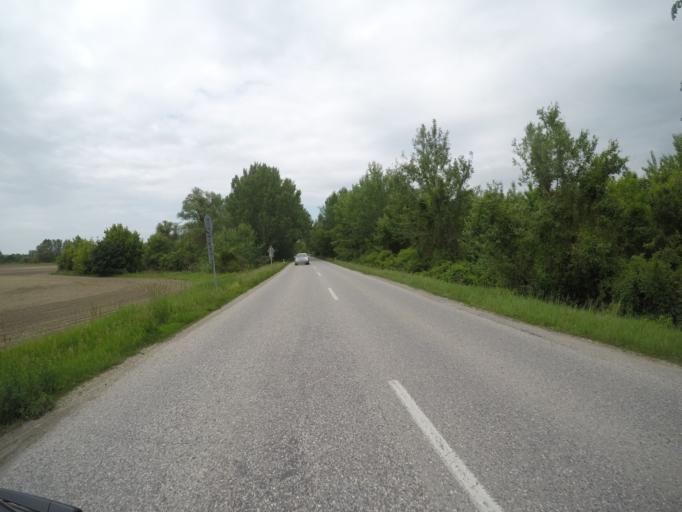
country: SK
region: Nitriansky
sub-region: Okres Nove Zamky
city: Sturovo
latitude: 47.8107
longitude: 18.7223
